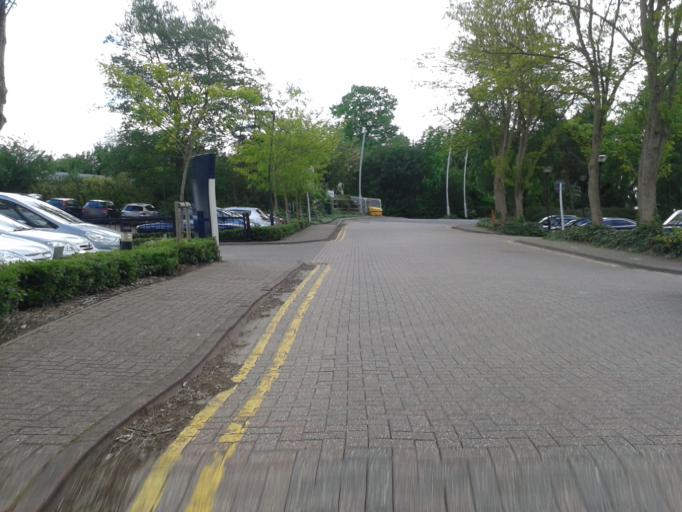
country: GB
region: England
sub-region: Cambridgeshire
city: Waterbeach
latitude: 52.2359
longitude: 0.1542
